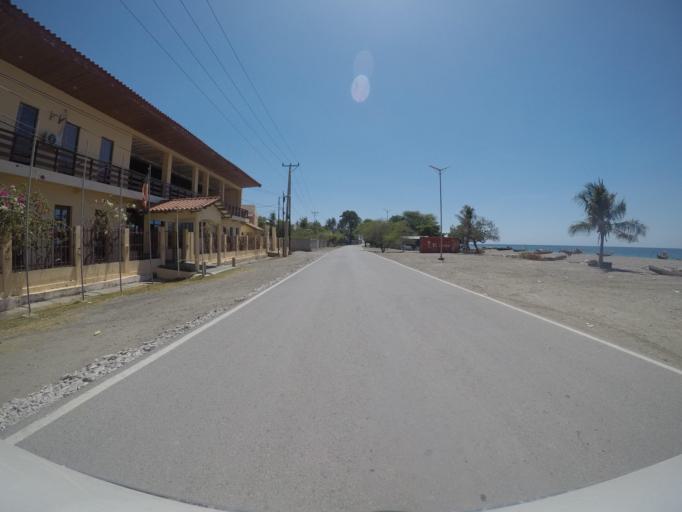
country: TL
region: Dili
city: Dili
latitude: -8.5400
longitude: 125.5387
